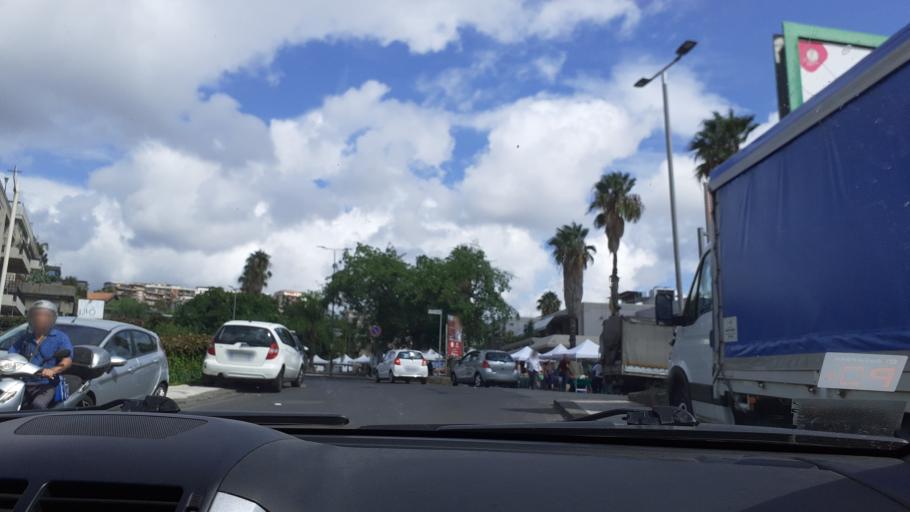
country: IT
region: Sicily
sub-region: Catania
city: Canalicchio
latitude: 37.5398
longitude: 15.0991
